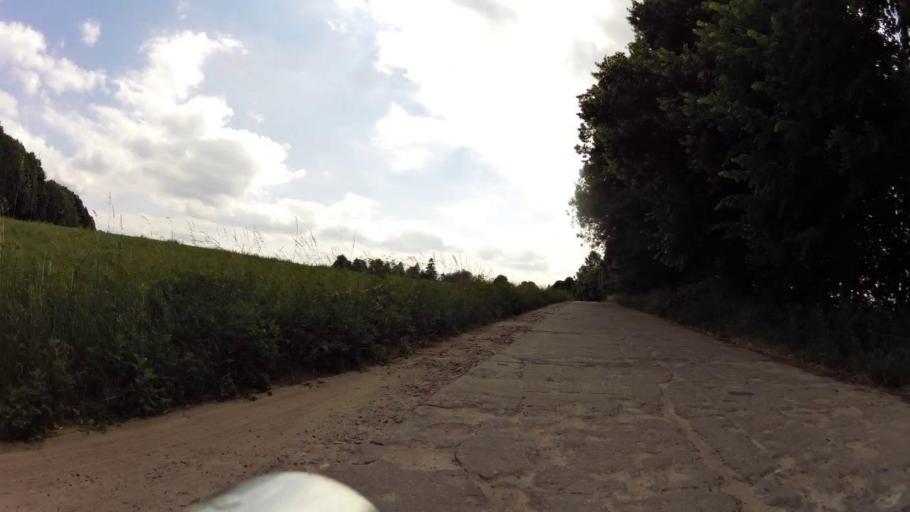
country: PL
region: West Pomeranian Voivodeship
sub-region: Powiat koszalinski
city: Bobolice
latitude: 53.9632
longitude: 16.6949
